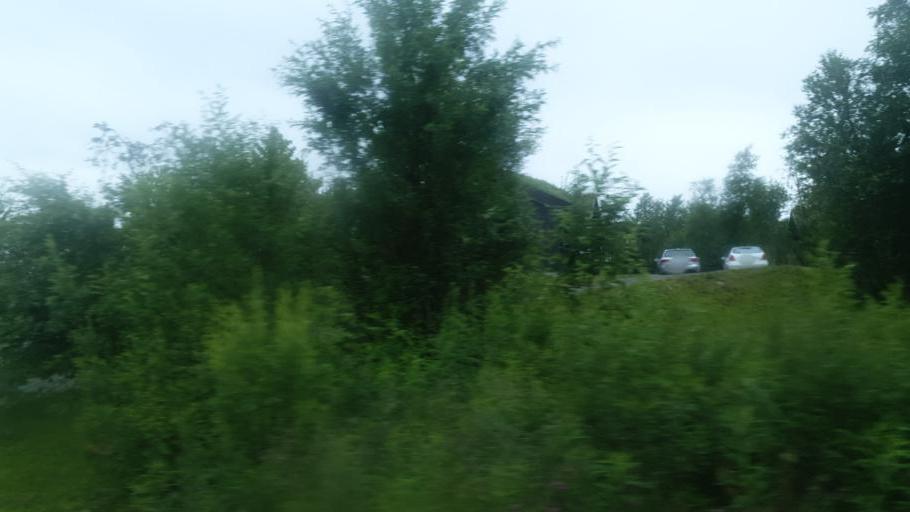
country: NO
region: Oppland
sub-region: Vestre Slidre
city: Slidre
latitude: 61.2394
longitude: 8.9166
